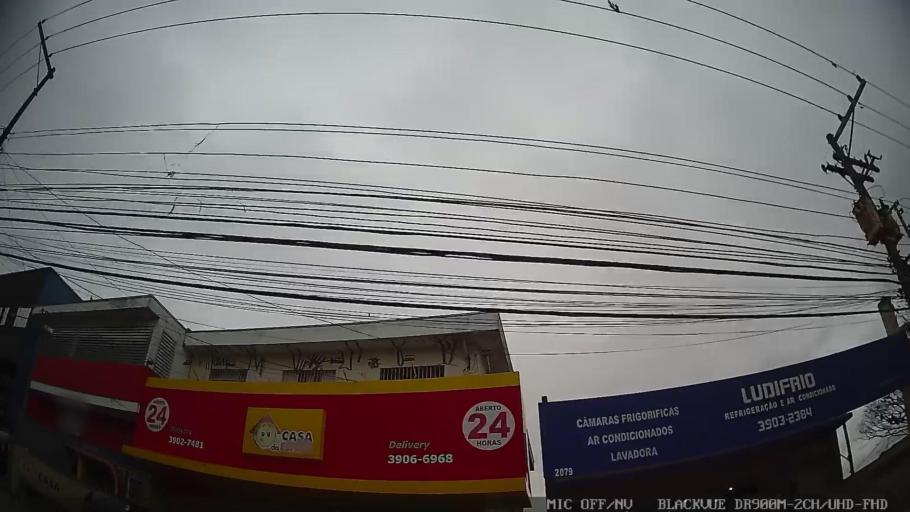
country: BR
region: Sao Paulo
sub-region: Osasco
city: Osasco
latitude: -23.4851
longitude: -46.7453
